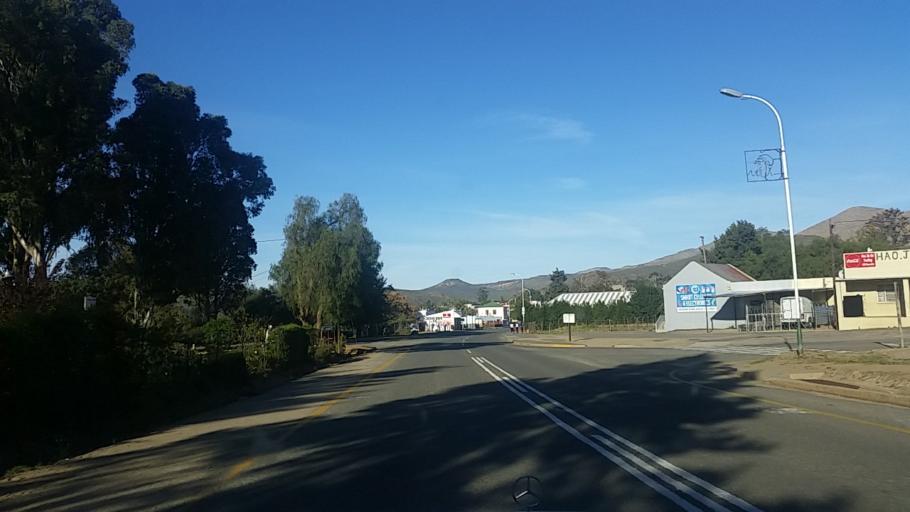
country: ZA
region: Western Cape
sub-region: Eden District Municipality
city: Knysna
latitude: -33.6592
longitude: 23.1170
